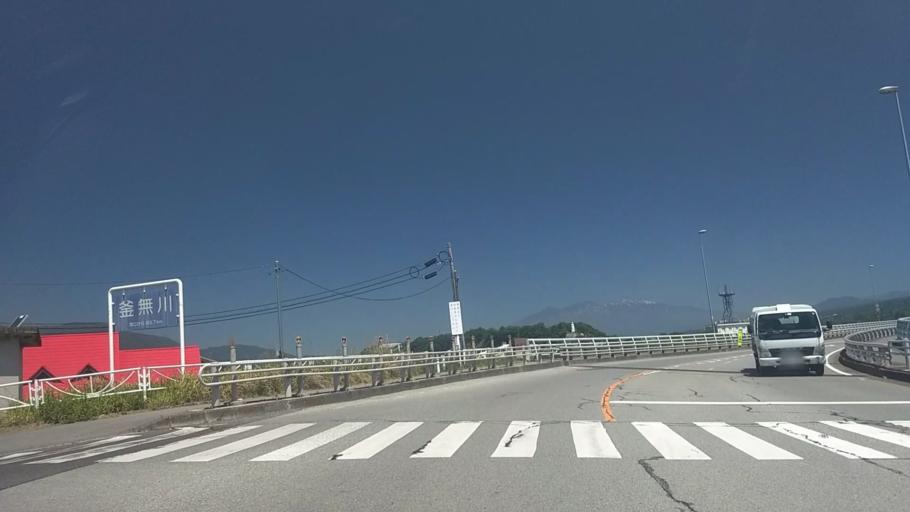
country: JP
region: Yamanashi
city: Nirasaki
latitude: 35.6989
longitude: 138.4535
